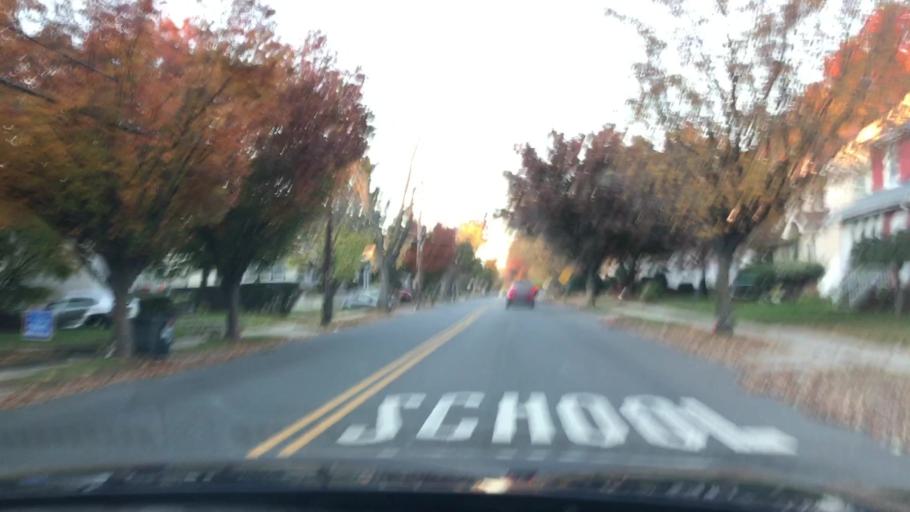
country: US
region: New Jersey
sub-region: Bergen County
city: Bogota
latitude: 40.8687
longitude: -74.0288
